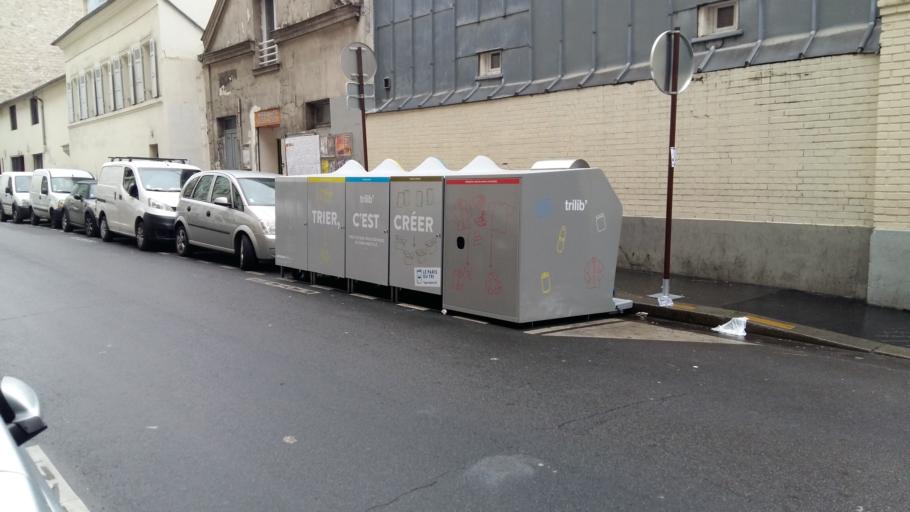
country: FR
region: Ile-de-France
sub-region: Paris
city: Saint-Ouen
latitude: 48.8934
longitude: 2.3600
